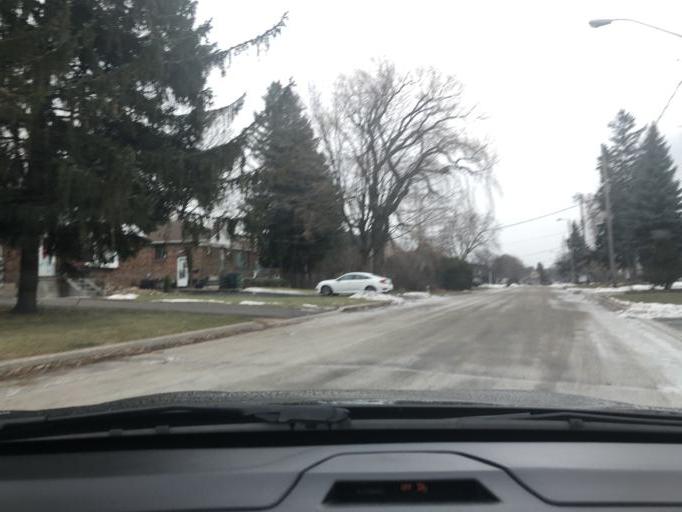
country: CA
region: Ontario
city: Scarborough
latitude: 43.7855
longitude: -79.2704
